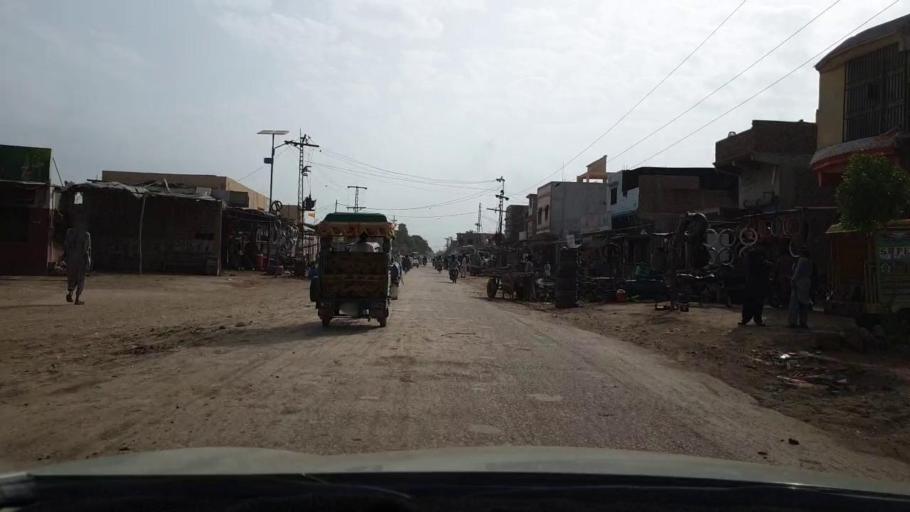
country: PK
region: Sindh
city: Matli
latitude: 25.0349
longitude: 68.6570
